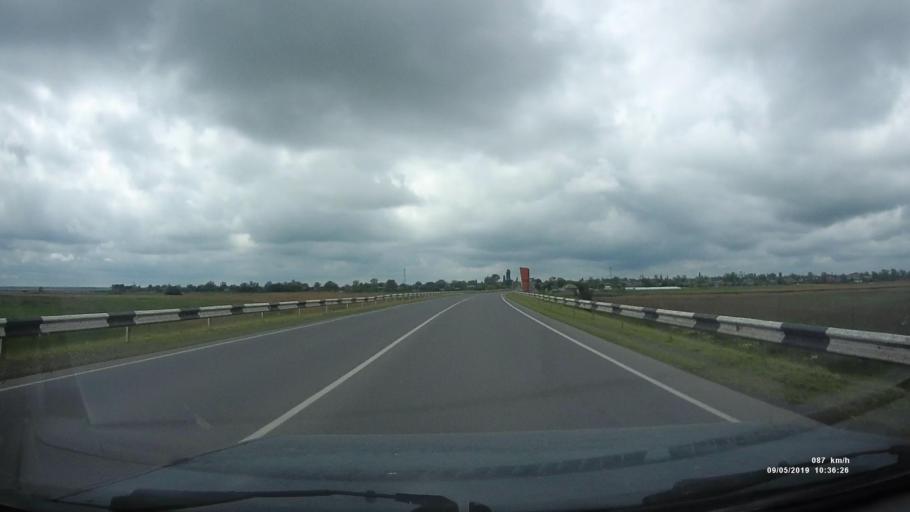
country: RU
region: Rostov
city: Peshkovo
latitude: 47.0315
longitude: 39.4093
